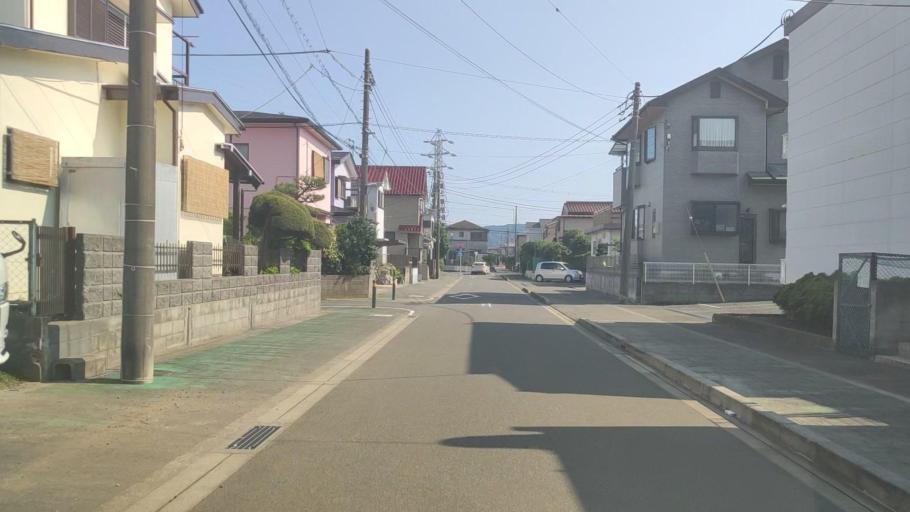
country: JP
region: Kanagawa
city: Hiratsuka
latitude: 35.3475
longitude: 139.3224
